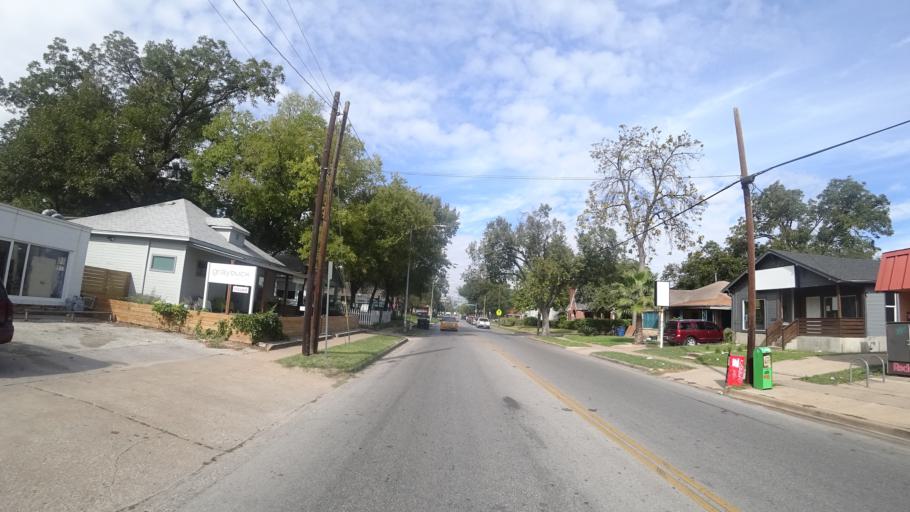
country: US
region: Texas
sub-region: Travis County
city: Austin
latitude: 30.2553
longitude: -97.7195
